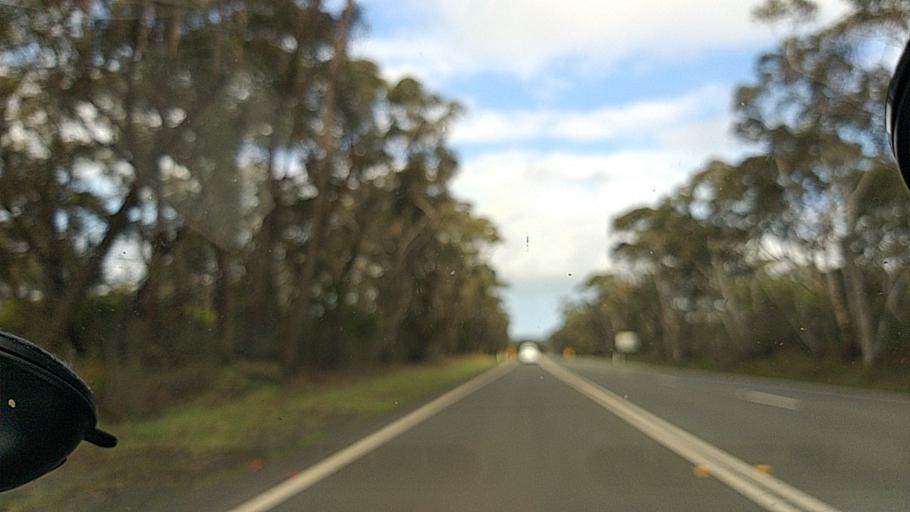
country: AU
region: New South Wales
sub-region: Wollongong
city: Bulli
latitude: -34.2641
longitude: 150.8862
